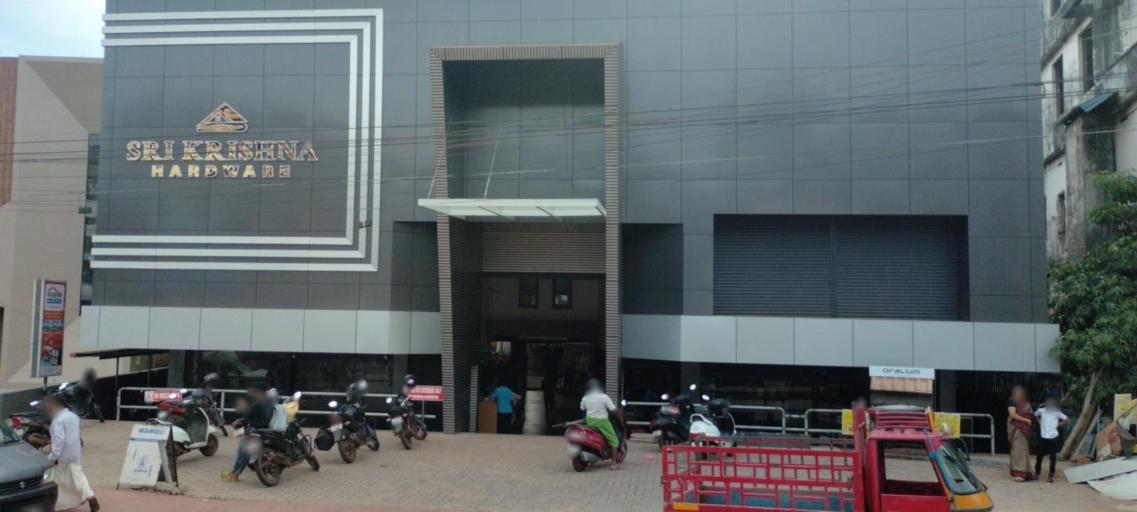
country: IN
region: Kerala
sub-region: Kasaragod District
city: Kasaragod
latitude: 12.5053
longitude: 74.9937
